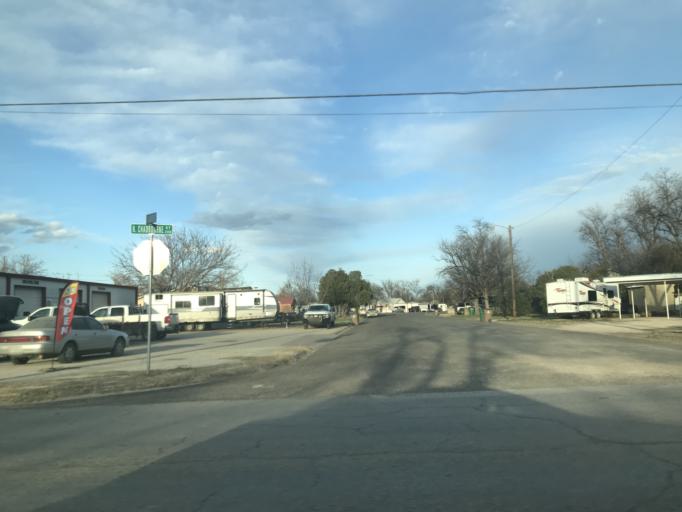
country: US
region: Texas
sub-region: Tom Green County
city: San Angelo
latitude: 31.4963
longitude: -100.4586
